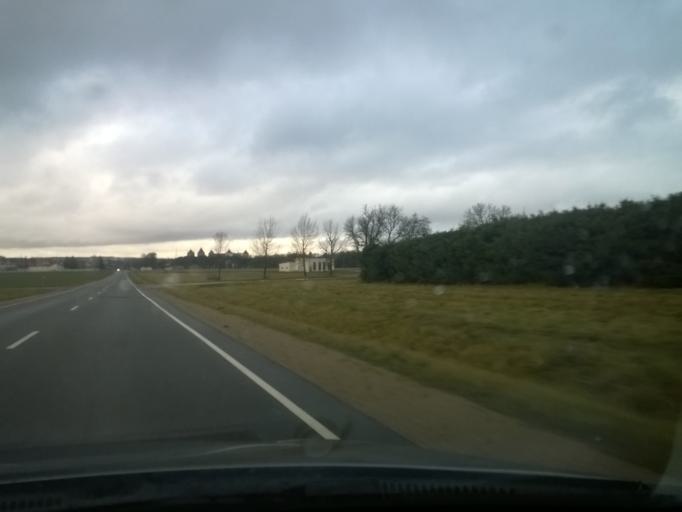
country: BY
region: Grodnenskaya
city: Mir
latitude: 53.4431
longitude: 26.4765
